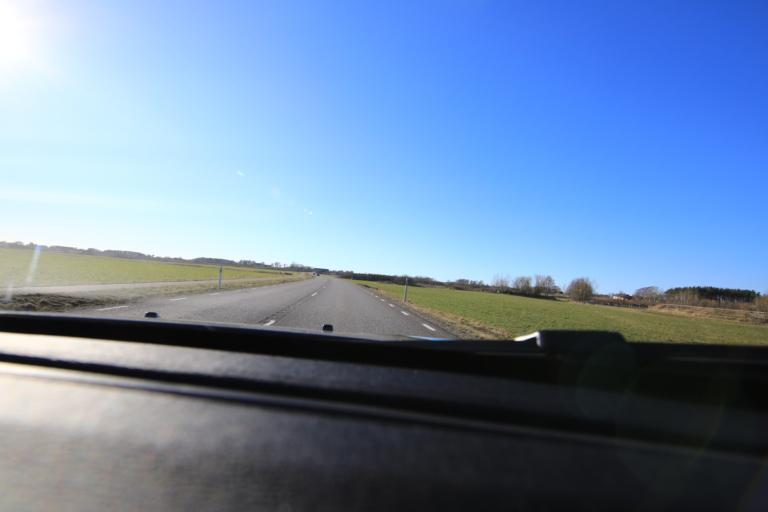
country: SE
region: Halland
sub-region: Varbergs Kommun
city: Tvaaker
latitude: 57.0483
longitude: 12.3458
